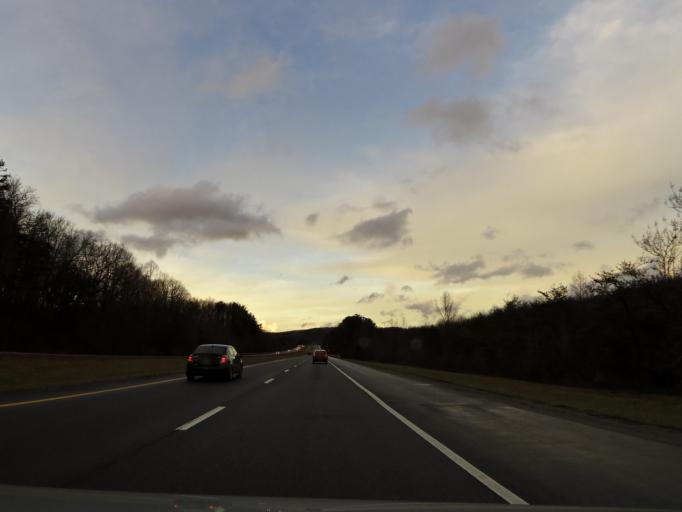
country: US
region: Tennessee
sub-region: Campbell County
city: Caryville
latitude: 36.3457
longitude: -84.2303
